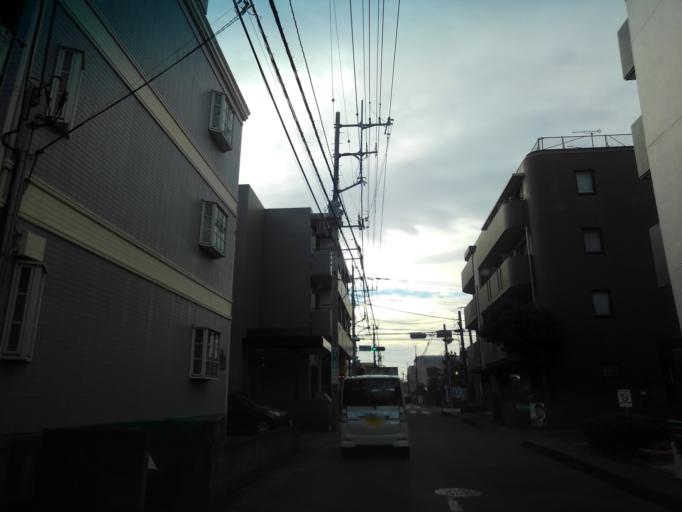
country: JP
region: Kanagawa
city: Minami-rinkan
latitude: 35.5051
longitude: 139.4455
